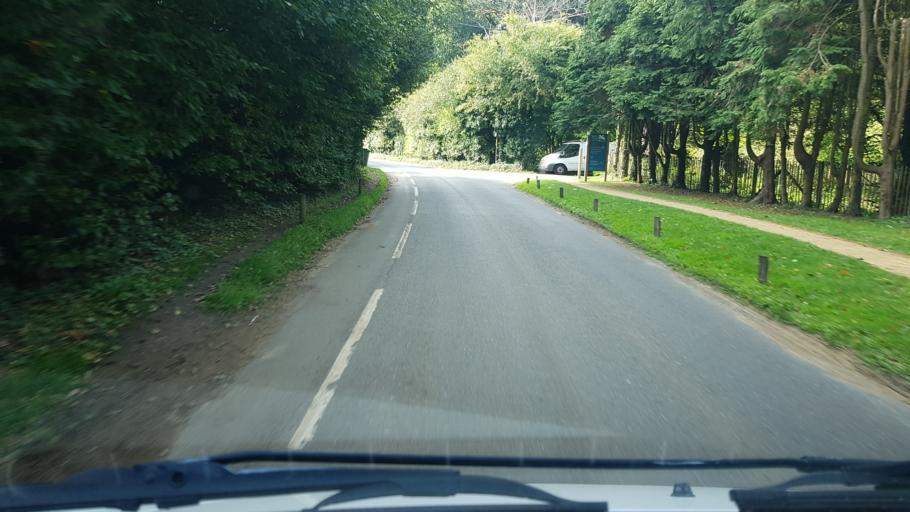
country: GB
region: England
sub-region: Surrey
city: Godalming
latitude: 51.2207
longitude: -0.6304
